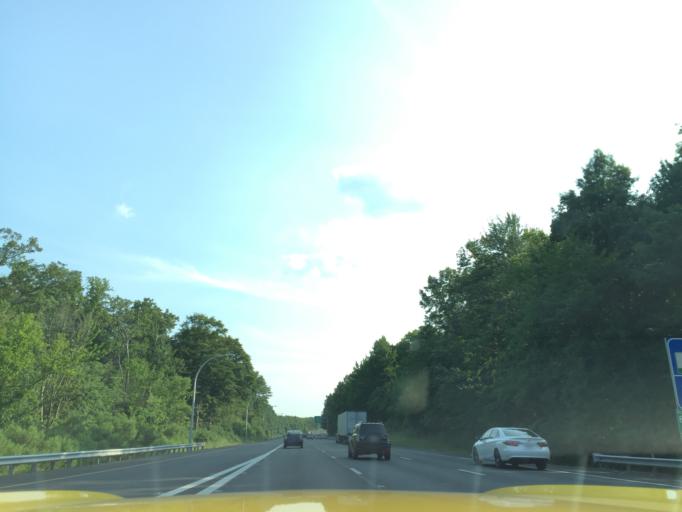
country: US
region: Maryland
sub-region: Harford County
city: Riverside
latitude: 39.4946
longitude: -76.2368
